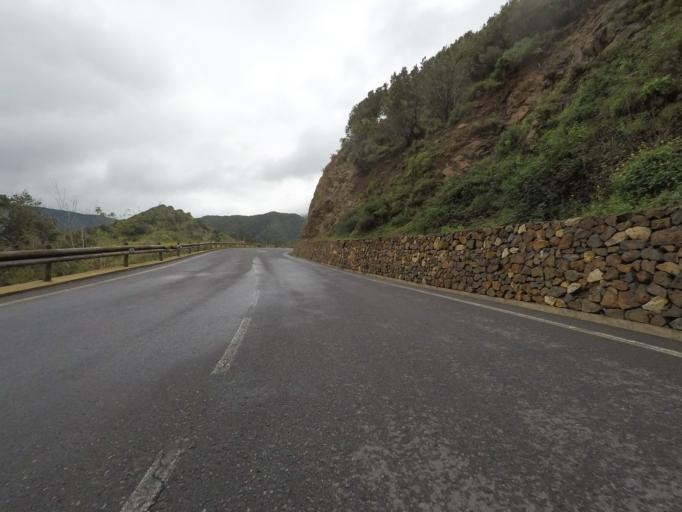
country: ES
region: Canary Islands
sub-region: Provincia de Santa Cruz de Tenerife
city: Vallehermosa
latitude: 28.1618
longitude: -17.2856
